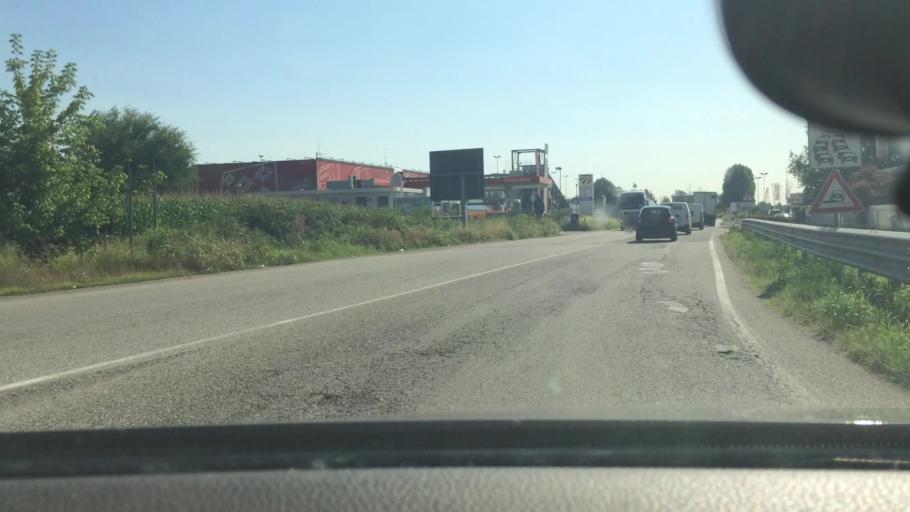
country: IT
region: Lombardy
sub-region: Citta metropolitana di Milano
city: Ossona
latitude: 45.5030
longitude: 8.9094
